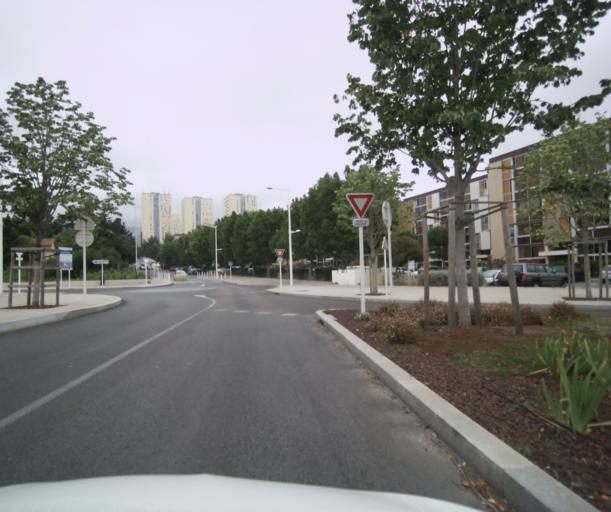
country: FR
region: Provence-Alpes-Cote d'Azur
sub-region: Departement du Var
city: La Seyne-sur-Mer
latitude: 43.1287
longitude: 5.8814
